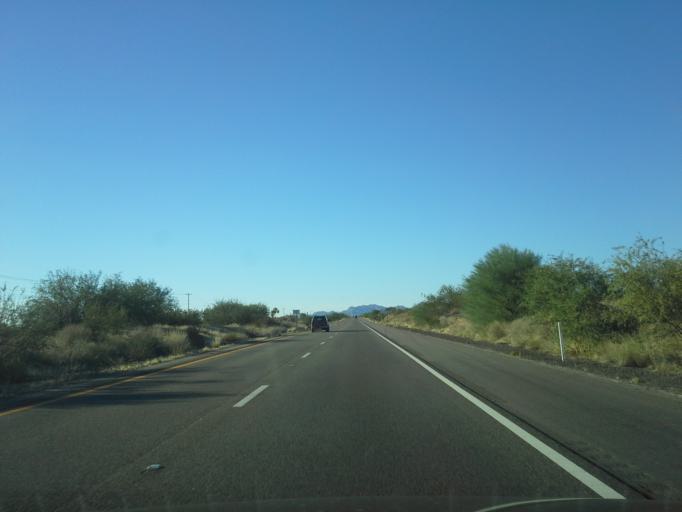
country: US
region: Arizona
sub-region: Pinal County
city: Gold Camp
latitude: 33.3293
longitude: -111.4329
